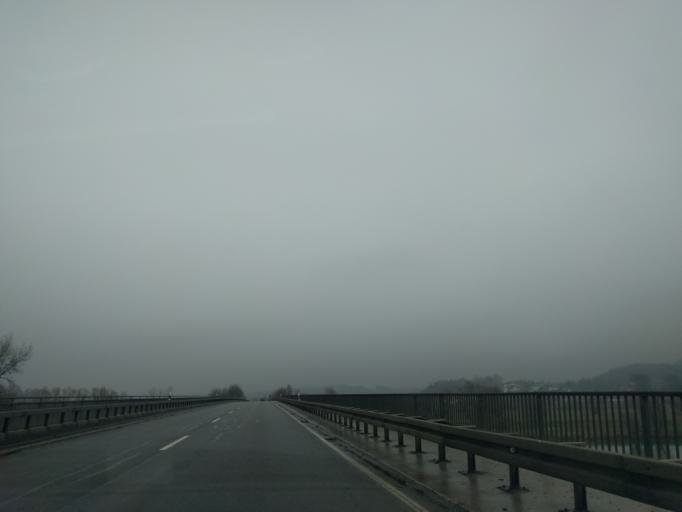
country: DE
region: Bavaria
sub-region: Lower Bavaria
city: Winzer
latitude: 48.7233
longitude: 13.0567
